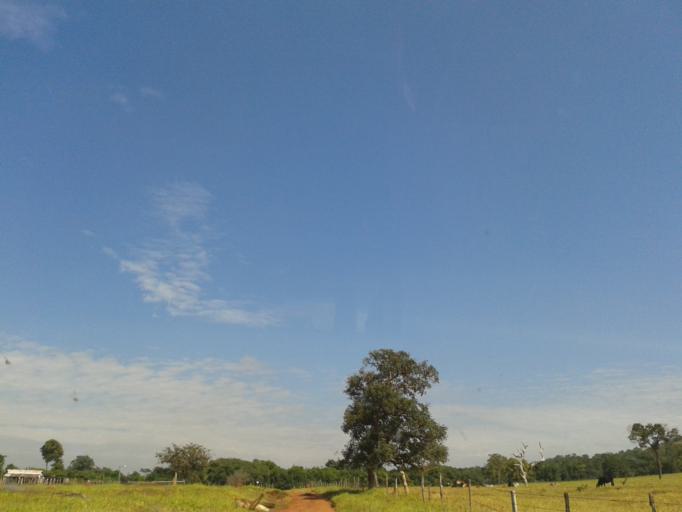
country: BR
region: Minas Gerais
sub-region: Campina Verde
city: Campina Verde
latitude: -19.3909
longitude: -49.6338
